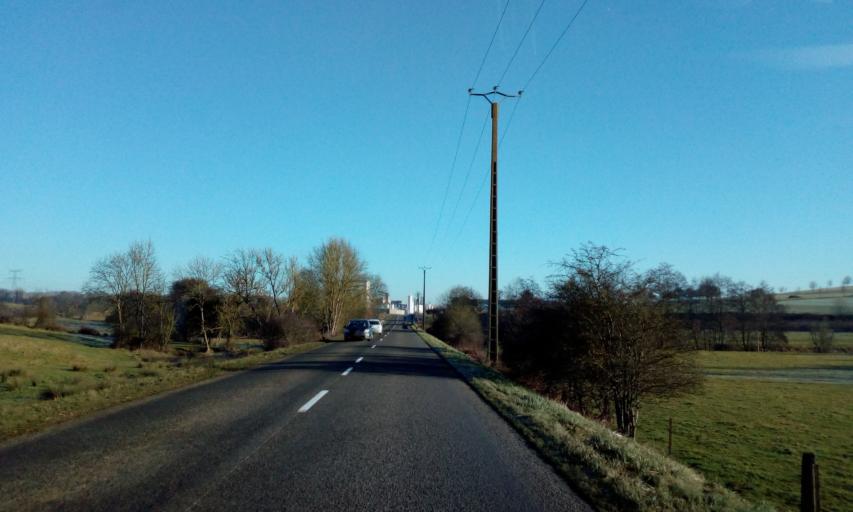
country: FR
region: Champagne-Ardenne
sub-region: Departement des Ardennes
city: Rimogne
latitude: 49.7842
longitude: 4.4725
